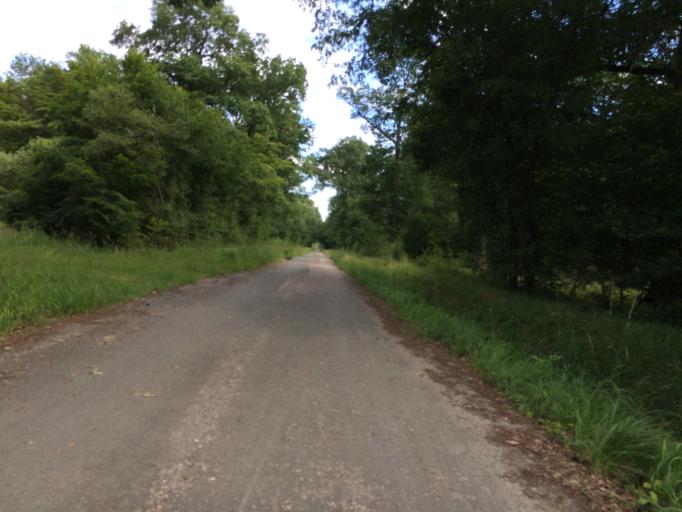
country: FR
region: Ile-de-France
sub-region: Departement de l'Essonne
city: Etiolles
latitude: 48.6615
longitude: 2.4833
